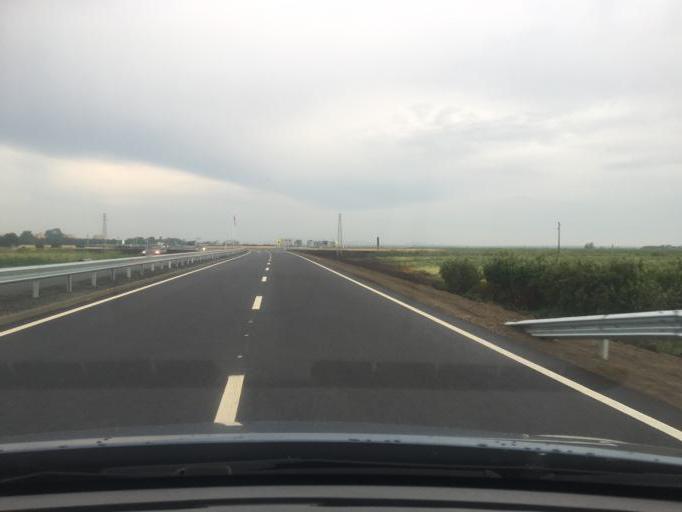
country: BG
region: Burgas
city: Aheloy
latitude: 42.6479
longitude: 27.6368
